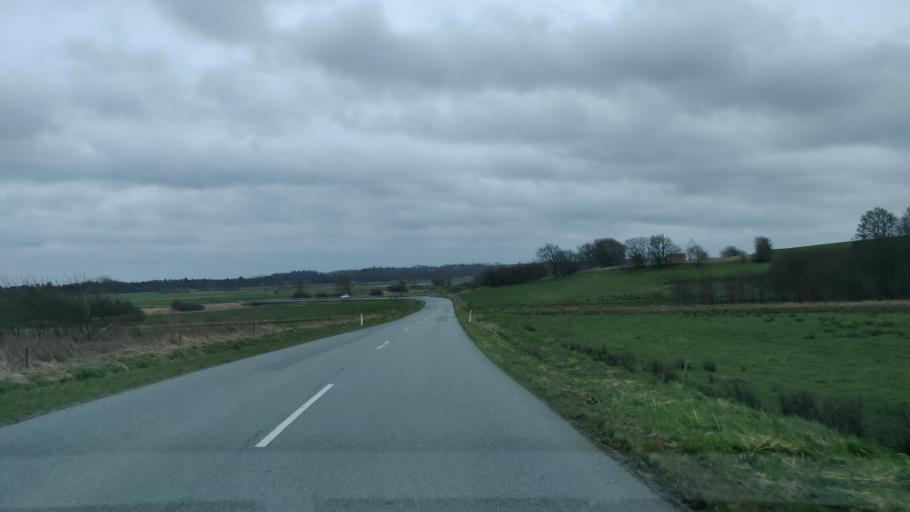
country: DK
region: Central Jutland
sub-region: Skive Kommune
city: Hojslev
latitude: 56.5725
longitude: 9.2364
